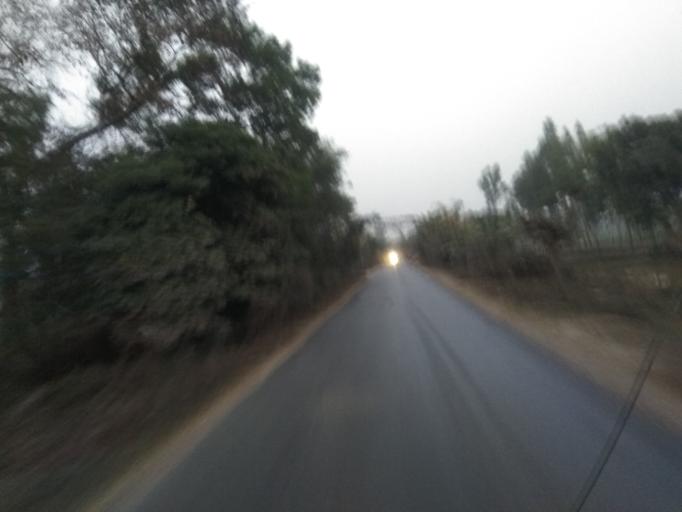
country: BD
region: Rajshahi
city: Bogra
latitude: 24.7483
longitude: 89.3406
